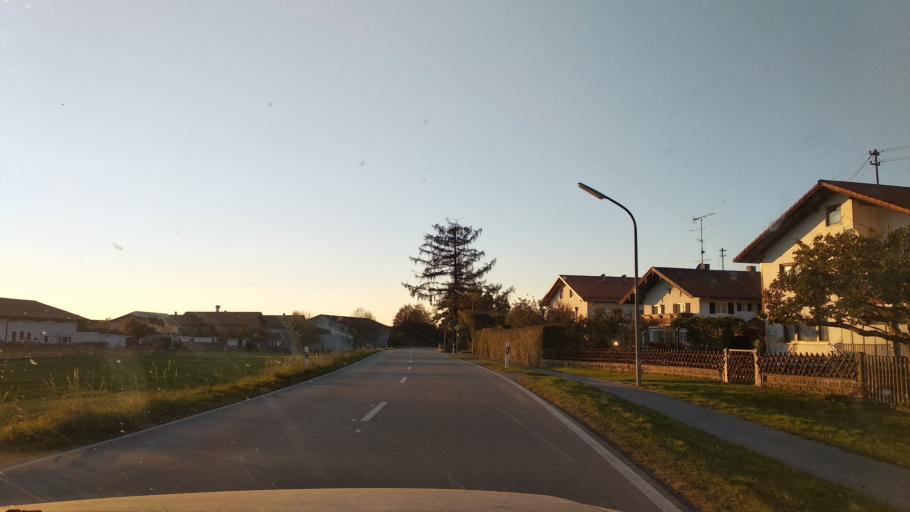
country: DE
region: Bavaria
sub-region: Upper Bavaria
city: Egmating
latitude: 48.0068
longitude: 11.7922
